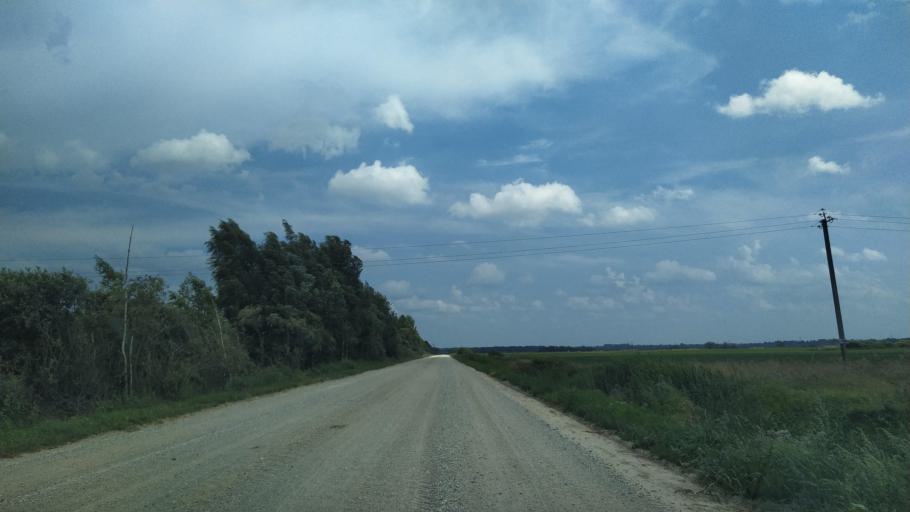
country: RU
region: Pskov
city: Pskov
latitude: 57.5851
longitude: 28.3224
